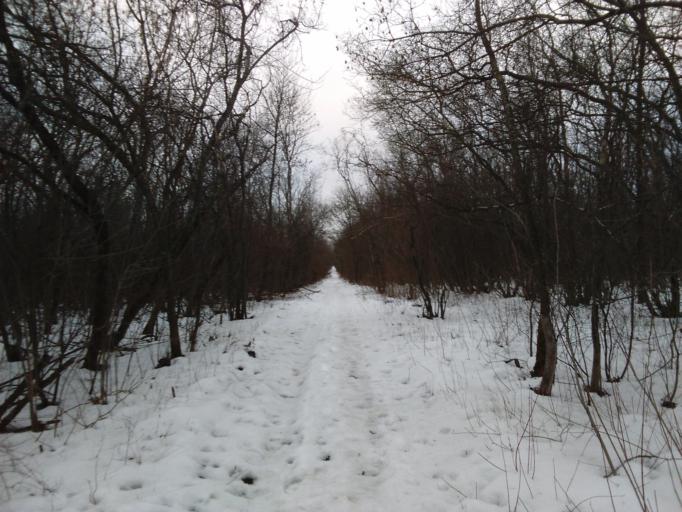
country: RU
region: Rostov
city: Temernik
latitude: 47.3516
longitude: 39.7396
